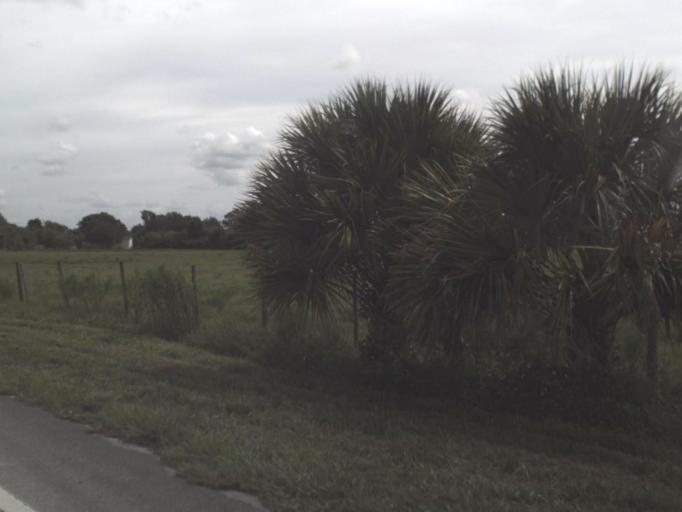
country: US
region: Florida
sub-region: Okeechobee County
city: Taylor Creek
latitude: 27.2581
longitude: -80.7476
